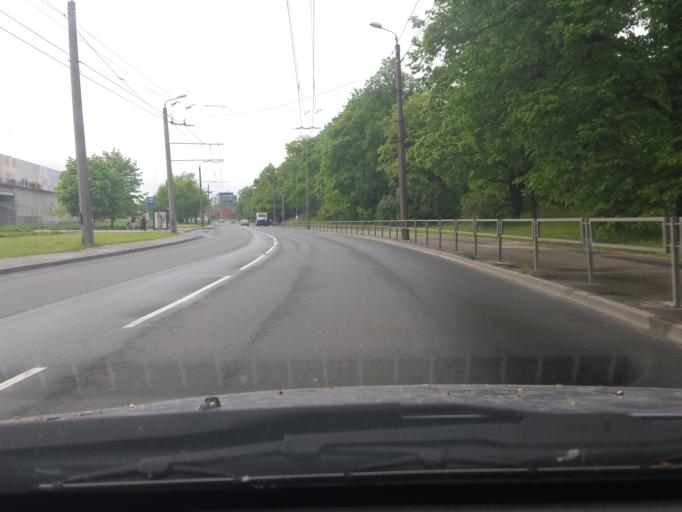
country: LV
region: Riga
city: Riga
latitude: 56.9861
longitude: 24.1345
